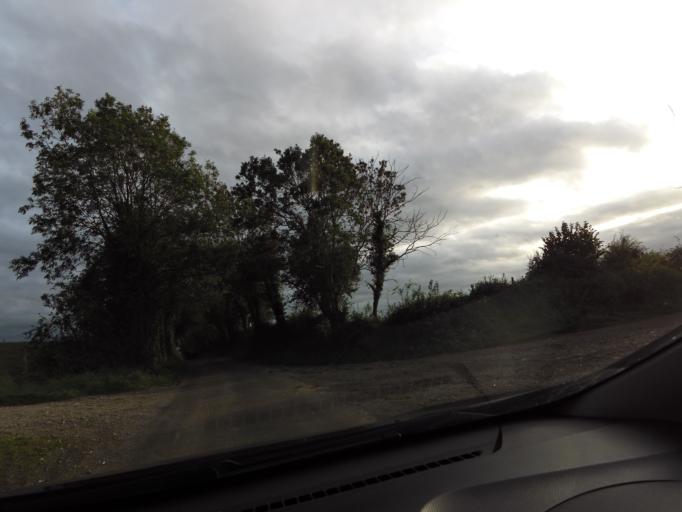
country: IE
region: Leinster
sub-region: Uibh Fhaili
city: Ferbane
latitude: 53.1847
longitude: -7.7272
